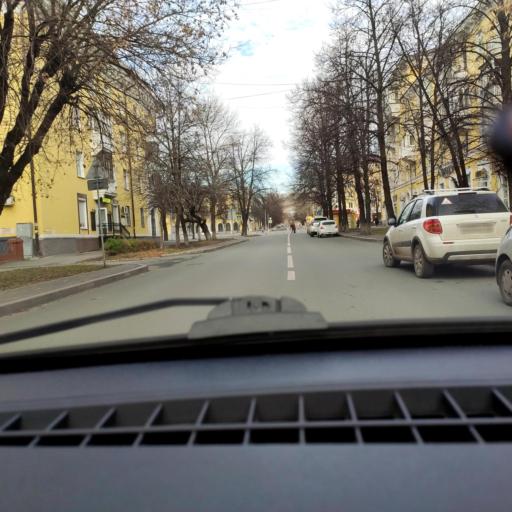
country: RU
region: Bashkortostan
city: Ufa
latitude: 54.8181
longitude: 56.0690
